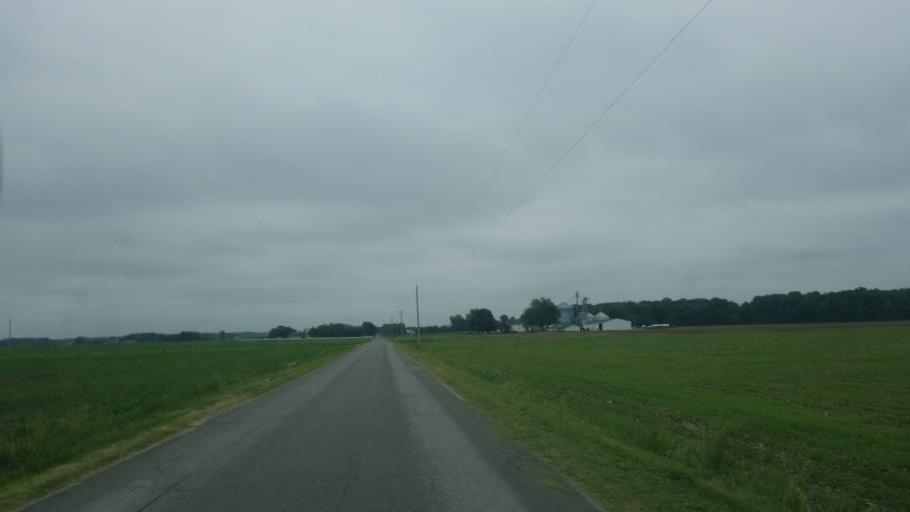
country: US
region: Indiana
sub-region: Elkhart County
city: Nappanee
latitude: 41.4717
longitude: -86.0422
